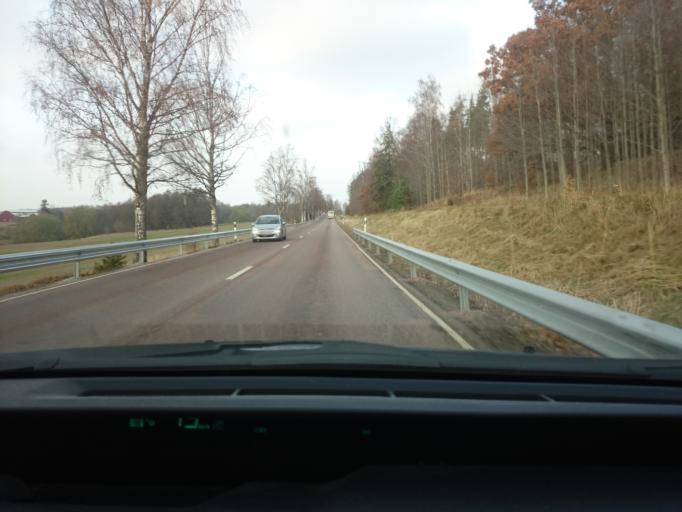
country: SE
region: Vaestmanland
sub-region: Vasteras
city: Skultuna
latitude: 59.6694
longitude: 16.4763
